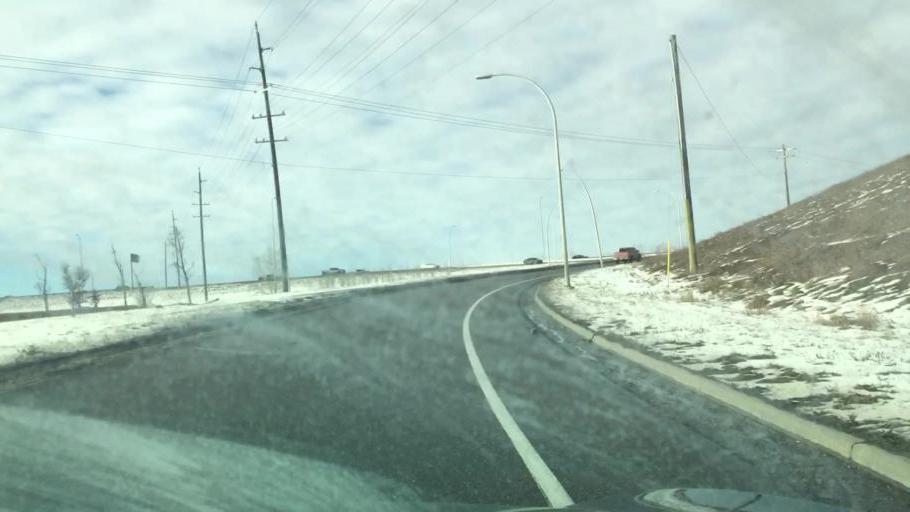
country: CA
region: Alberta
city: Calgary
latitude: 50.9950
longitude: -114.0484
